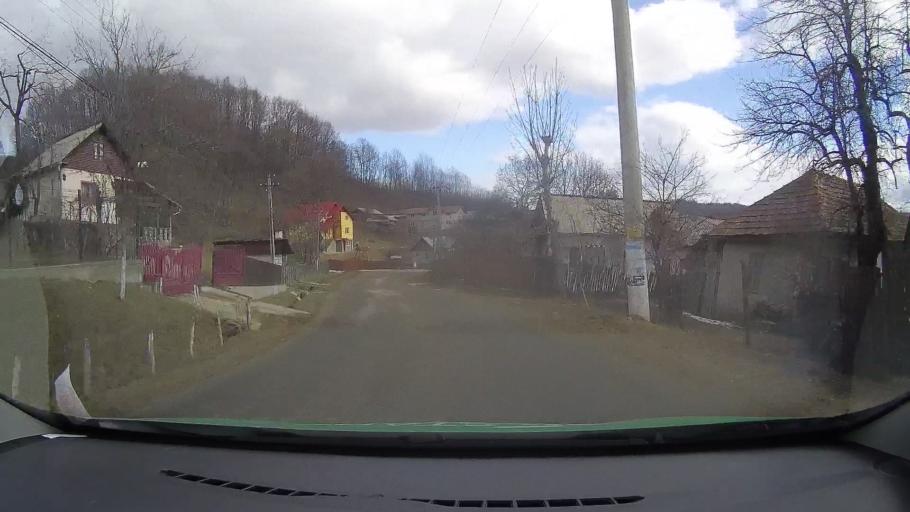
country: RO
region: Dambovita
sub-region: Comuna Buciumeni
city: Buciumeni
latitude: 45.1208
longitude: 25.4598
